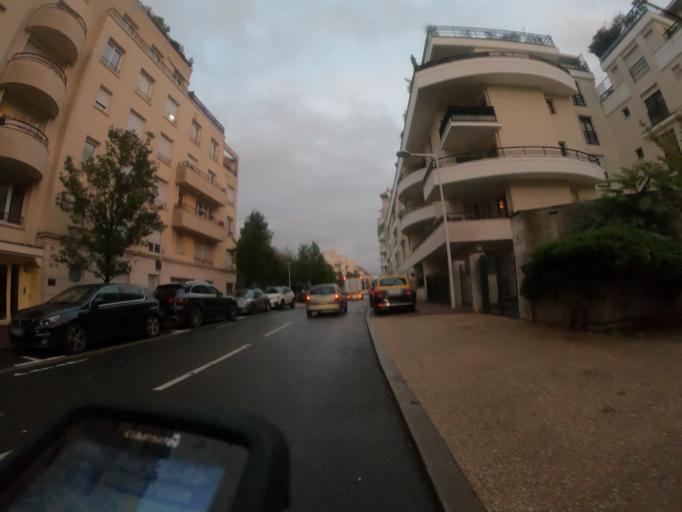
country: FR
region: Ile-de-France
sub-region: Departement des Hauts-de-Seine
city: Issy-les-Moulineaux
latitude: 48.8217
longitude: 2.2770
